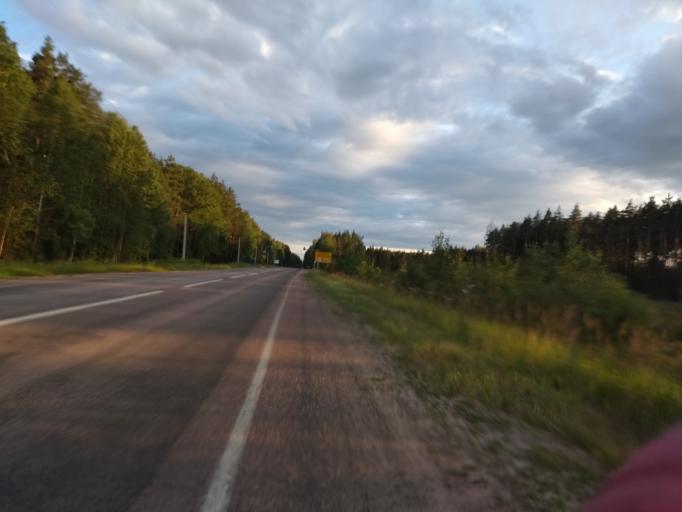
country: RU
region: Moskovskaya
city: Misheronskiy
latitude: 55.6198
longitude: 39.7278
